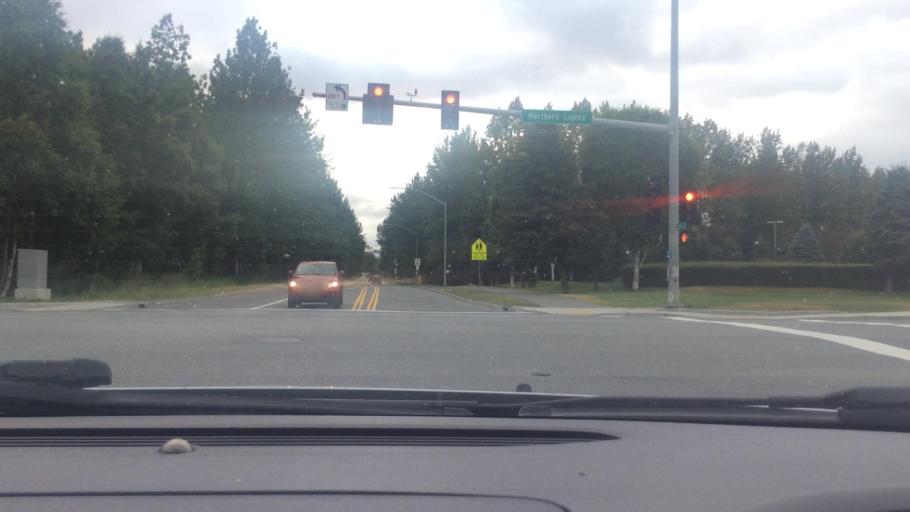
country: US
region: Alaska
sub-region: Anchorage Municipality
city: Anchorage
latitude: 61.1951
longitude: -149.7634
